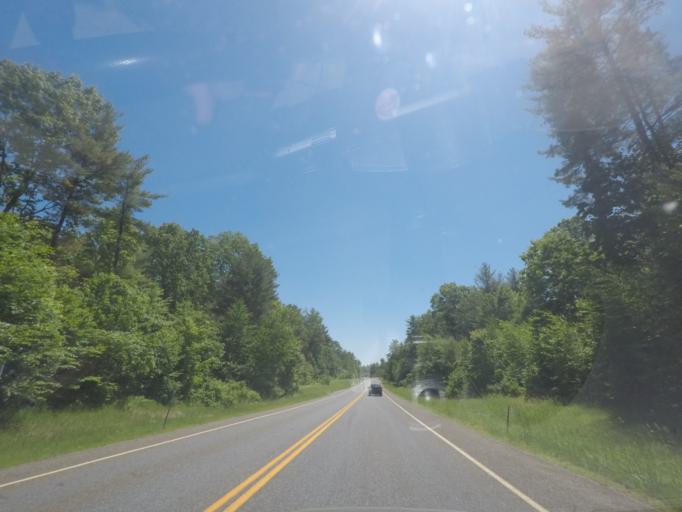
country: US
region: New York
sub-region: Saratoga County
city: Country Knolls
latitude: 42.9482
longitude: -73.7433
